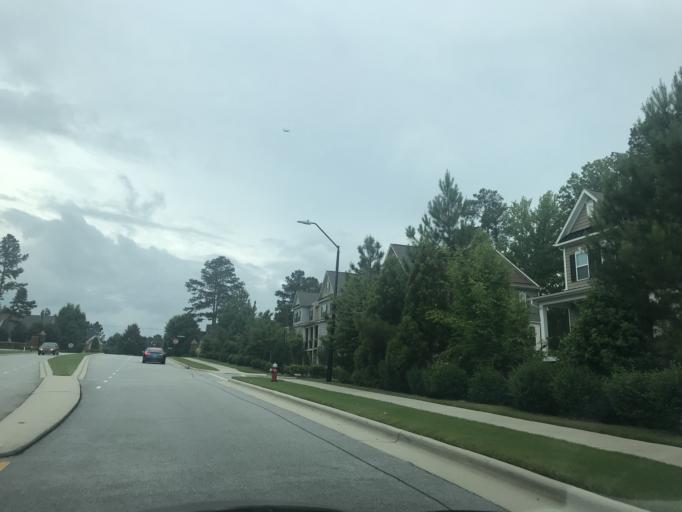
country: US
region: North Carolina
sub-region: Wake County
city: Green Level
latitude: 35.8065
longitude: -78.8862
